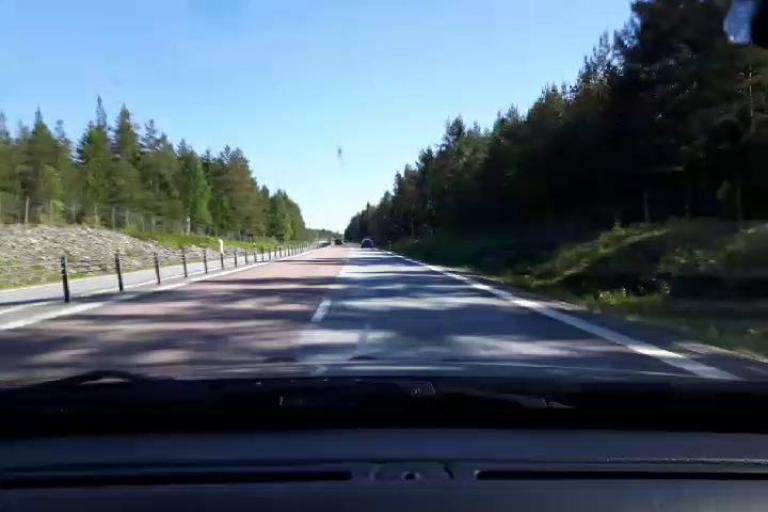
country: SE
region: Gaevleborg
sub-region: Gavle Kommun
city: Norrsundet
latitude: 60.8573
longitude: 17.0643
